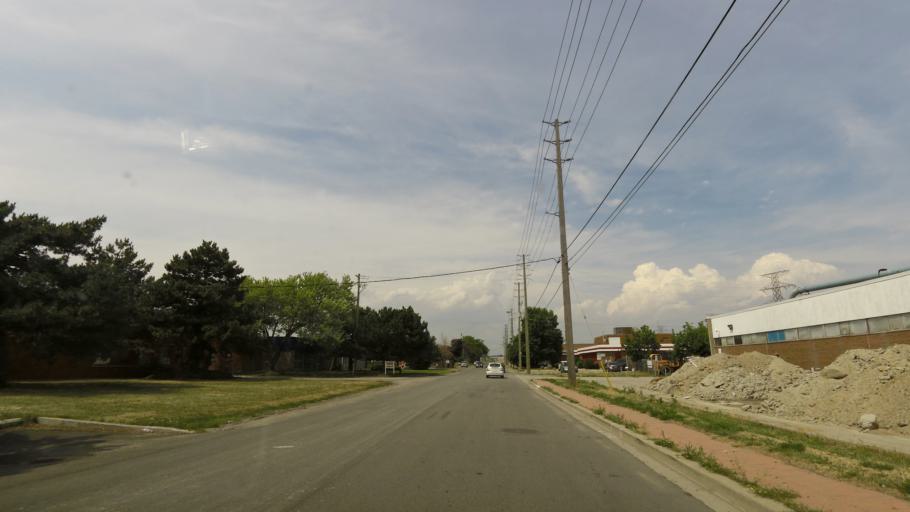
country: CA
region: Ontario
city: Etobicoke
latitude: 43.6210
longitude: -79.5347
